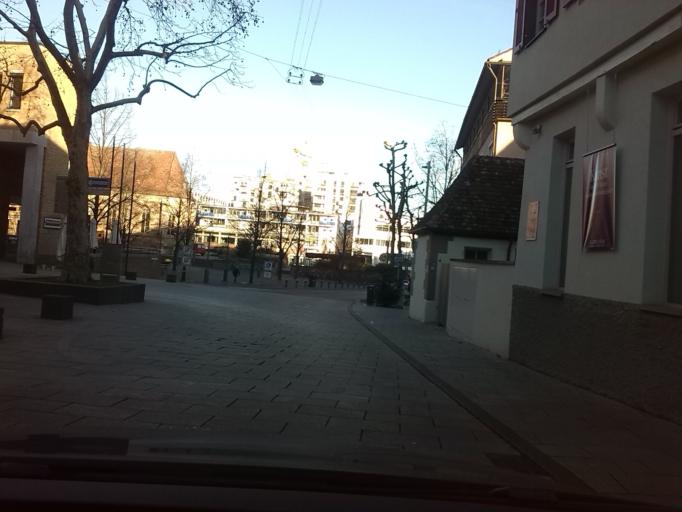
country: DE
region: Baden-Wuerttemberg
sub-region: Regierungsbezirk Stuttgart
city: Fellbach
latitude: 48.8078
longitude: 9.2770
